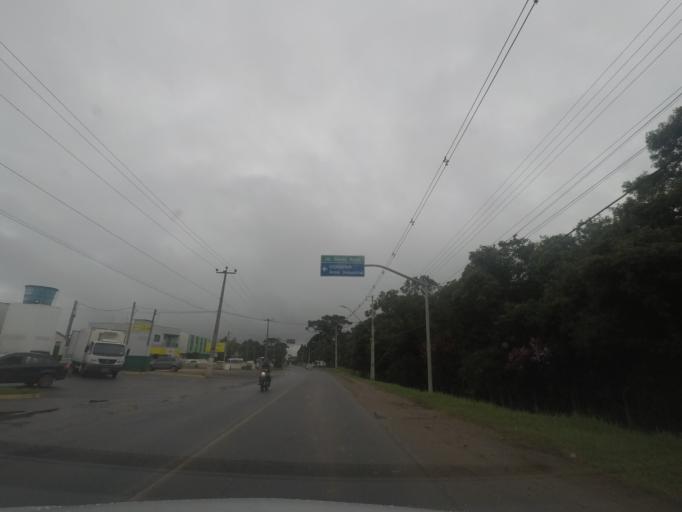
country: BR
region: Parana
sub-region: Quatro Barras
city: Quatro Barras
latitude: -25.3453
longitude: -49.0841
